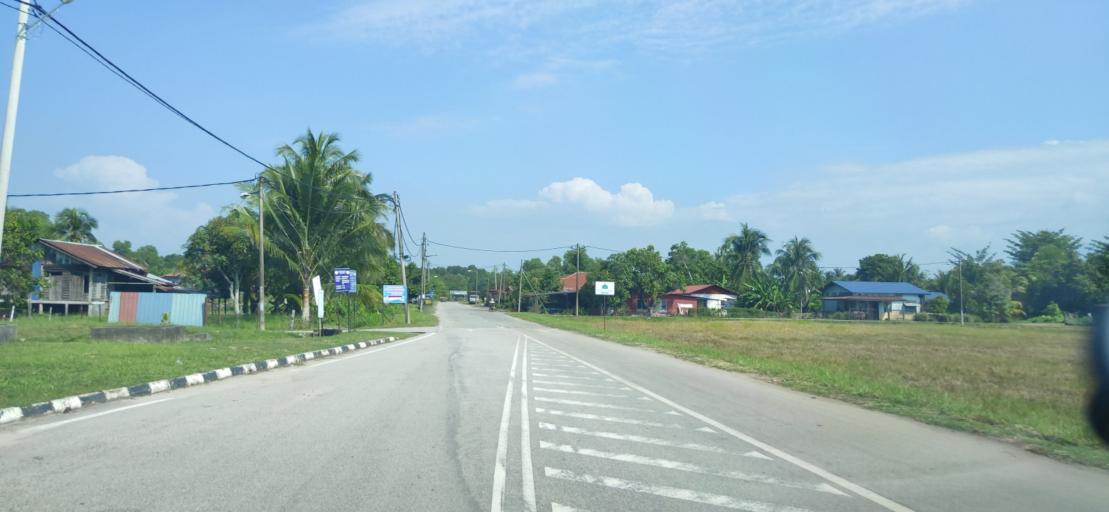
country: MY
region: Kedah
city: Sungai Petani
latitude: 5.6614
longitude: 100.4627
